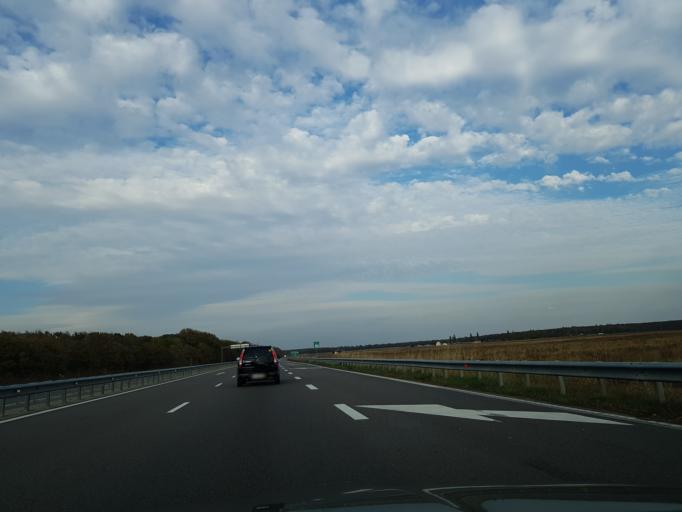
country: RO
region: Ilfov
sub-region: Comuna Snagov
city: Snagov
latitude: 44.6779
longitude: 26.2085
